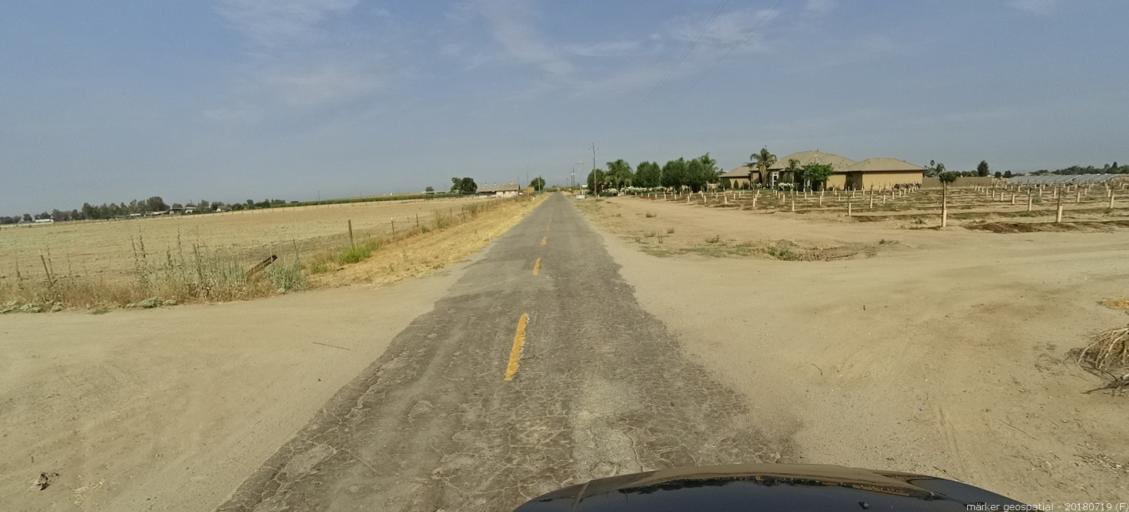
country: US
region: California
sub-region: Madera County
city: Fairmead
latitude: 37.0909
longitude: -120.2021
